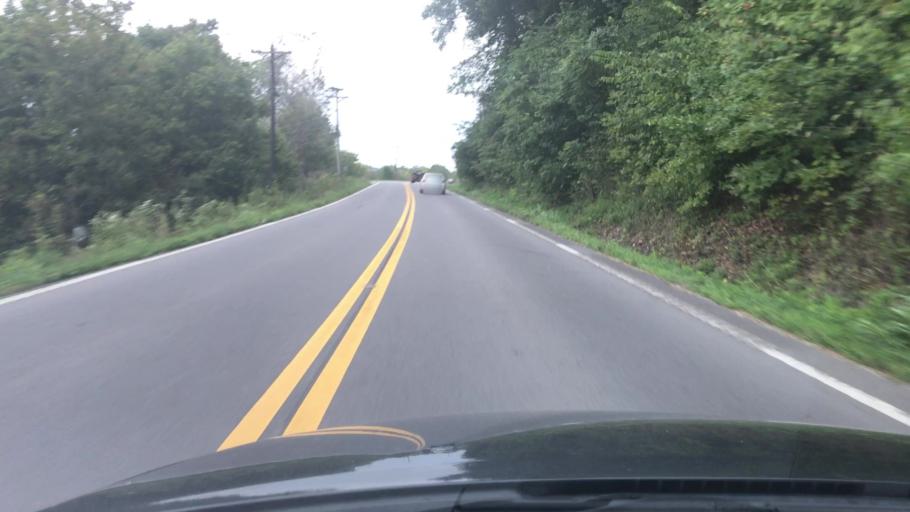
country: US
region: Tennessee
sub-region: Cheatham County
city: Ashland City
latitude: 36.2728
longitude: -87.0850
